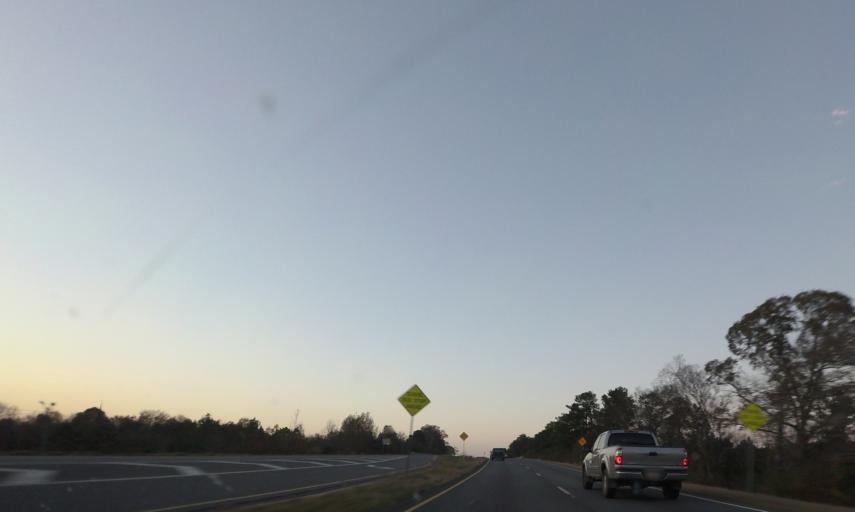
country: US
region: Georgia
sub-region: Houston County
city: Centerville
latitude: 32.7183
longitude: -83.6499
